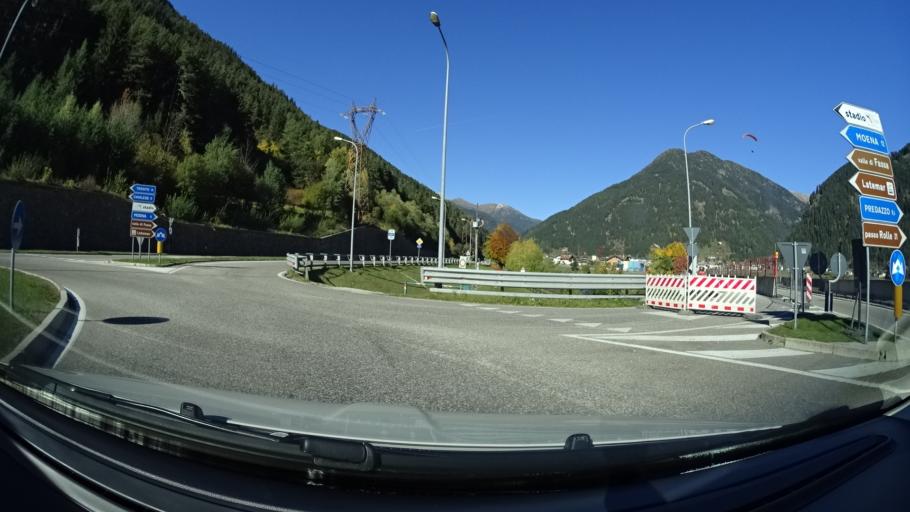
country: IT
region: Trentino-Alto Adige
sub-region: Provincia di Trento
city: Predazzo
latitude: 46.3013
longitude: 11.5899
